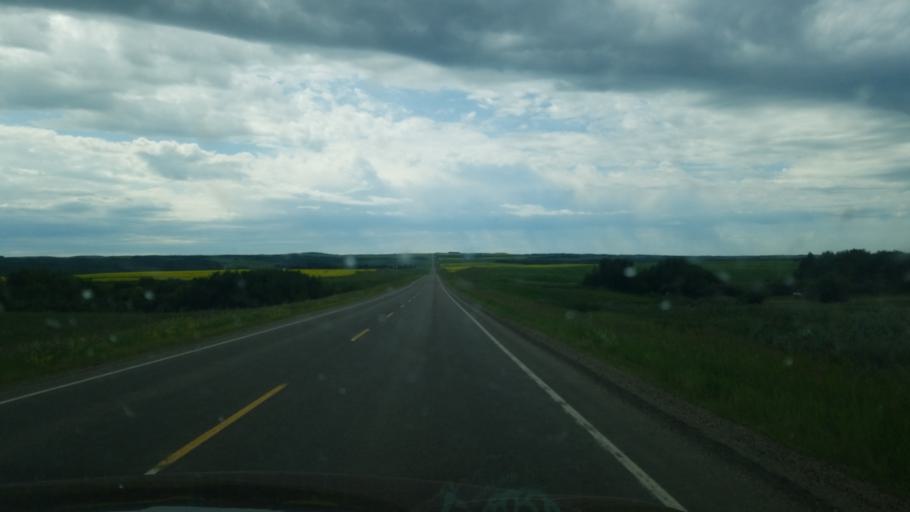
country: CA
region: Saskatchewan
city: Unity
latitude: 52.9187
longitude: -109.3425
